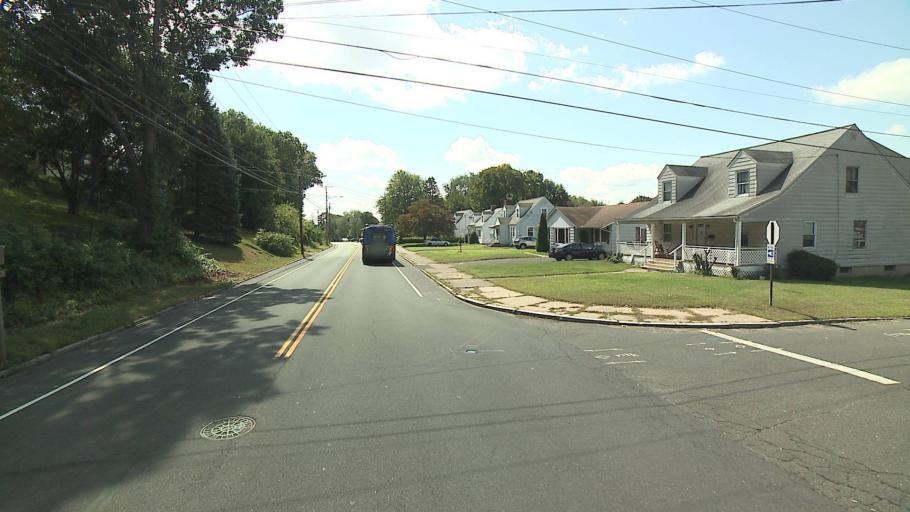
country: US
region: Connecticut
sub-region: New Haven County
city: Ansonia
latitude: 41.3566
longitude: -73.0811
